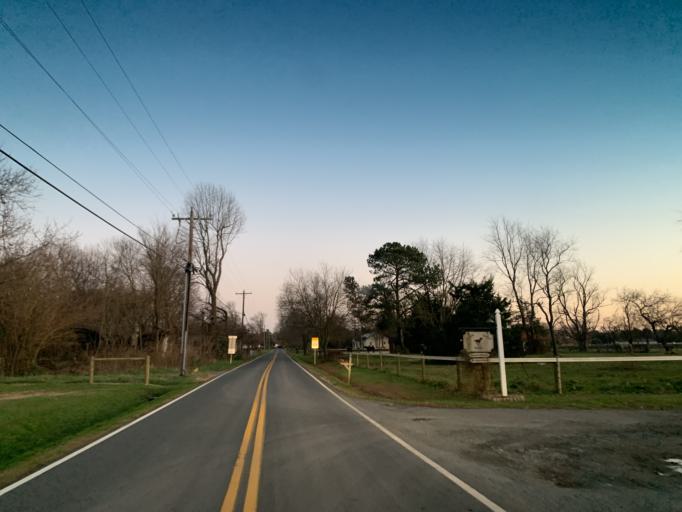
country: US
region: Delaware
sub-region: New Castle County
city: Middletown
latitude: 39.4198
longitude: -75.7818
